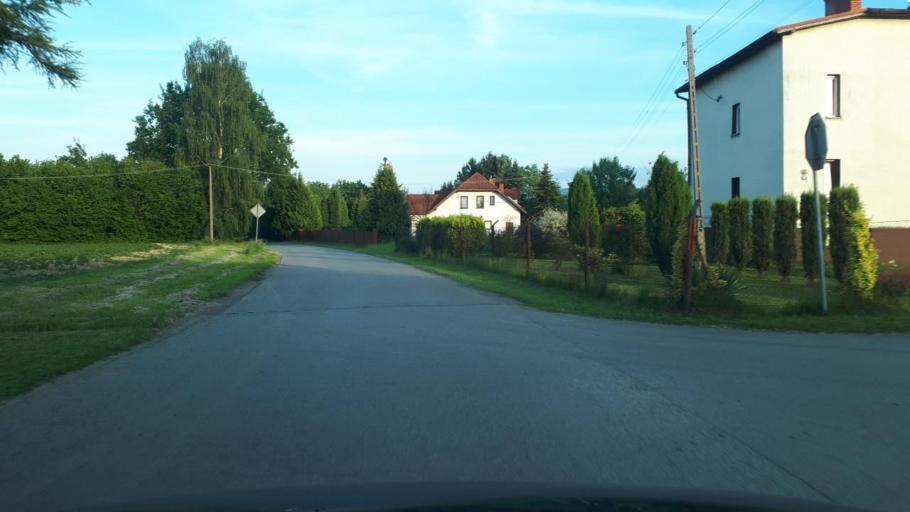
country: PL
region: Silesian Voivodeship
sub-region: Powiat bielski
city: Bronow
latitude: 49.8750
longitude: 18.9235
